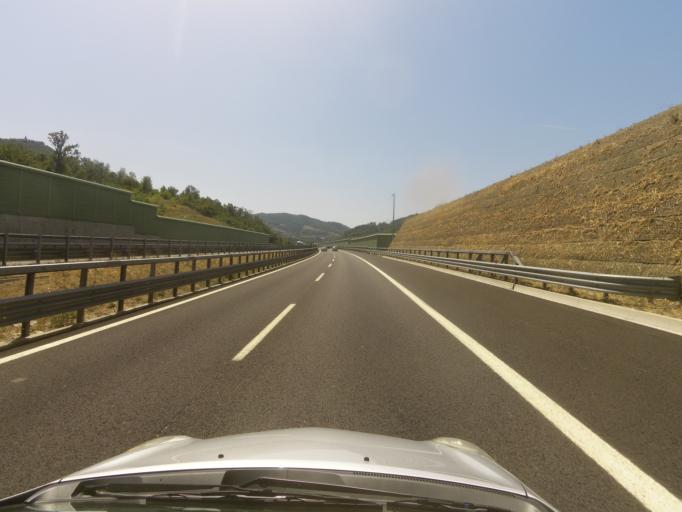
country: IT
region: Emilia-Romagna
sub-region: Provincia di Bologna
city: Grizzana
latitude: 44.2386
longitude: 11.1864
